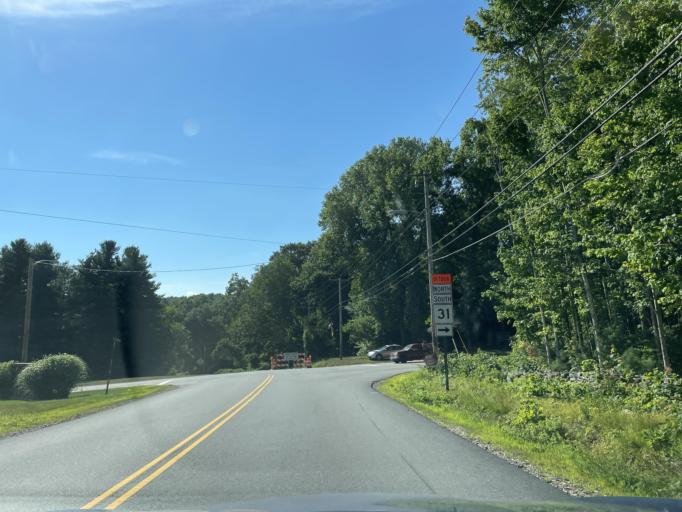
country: US
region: Massachusetts
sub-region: Worcester County
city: Charlton
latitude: 42.1344
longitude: -71.9412
